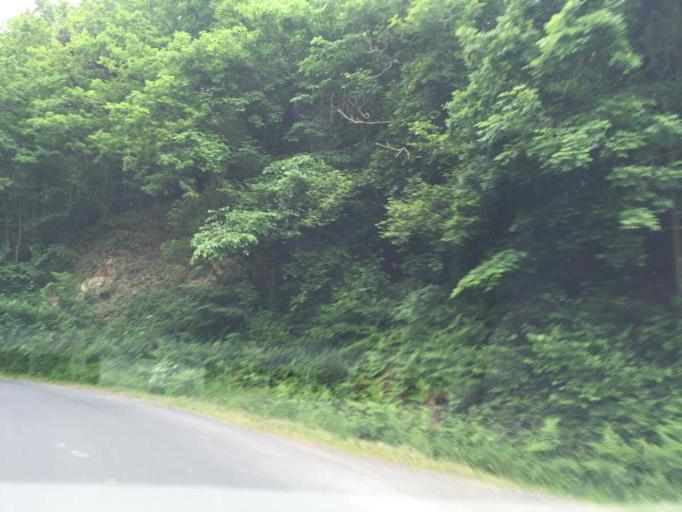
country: FR
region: Auvergne
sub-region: Departement du Puy-de-Dome
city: Ambert
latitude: 45.5460
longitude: 3.7736
